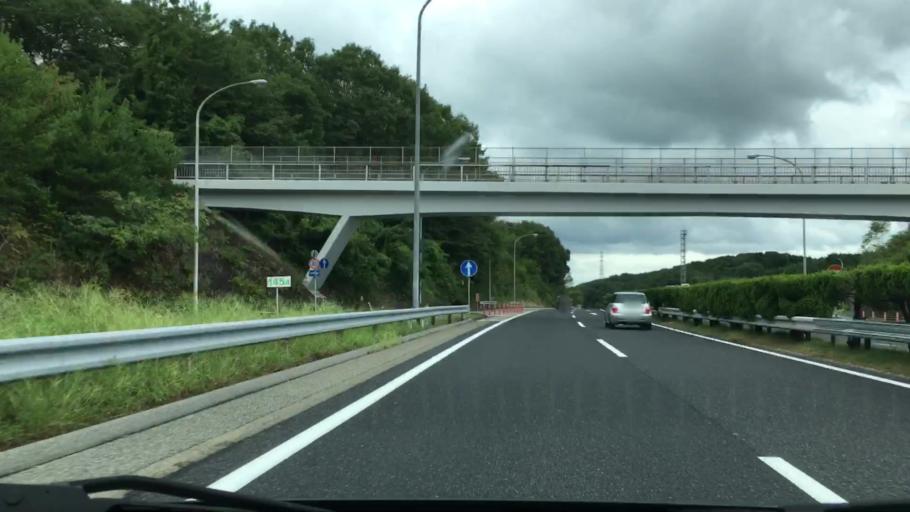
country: JP
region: Okayama
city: Tsuyama
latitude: 35.0443
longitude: 134.1038
